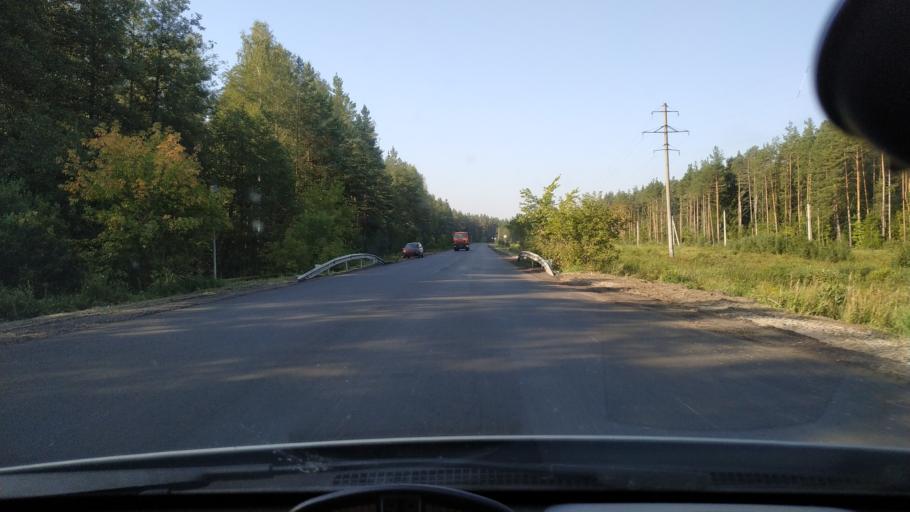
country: RU
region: Moskovskaya
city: Kerva
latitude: 55.5739
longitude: 39.6791
